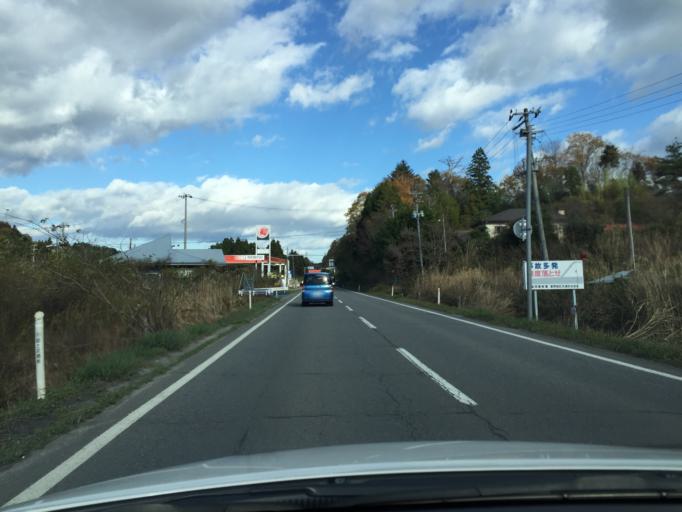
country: JP
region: Fukushima
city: Namie
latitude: 37.3735
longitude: 141.0091
